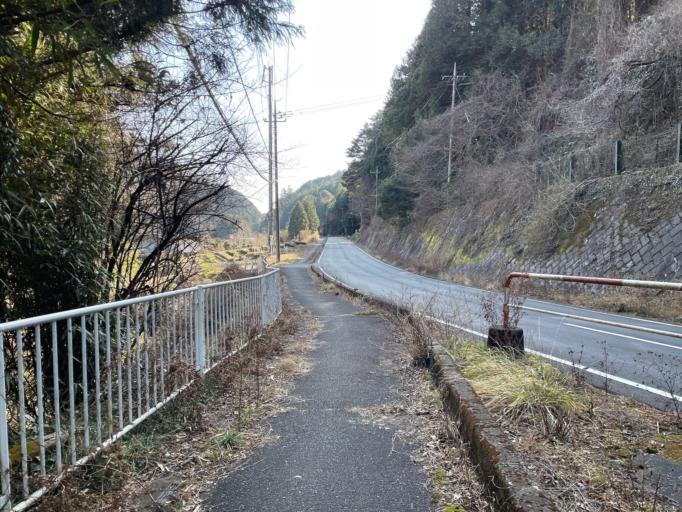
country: JP
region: Saitama
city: Hanno
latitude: 35.8522
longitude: 139.2512
